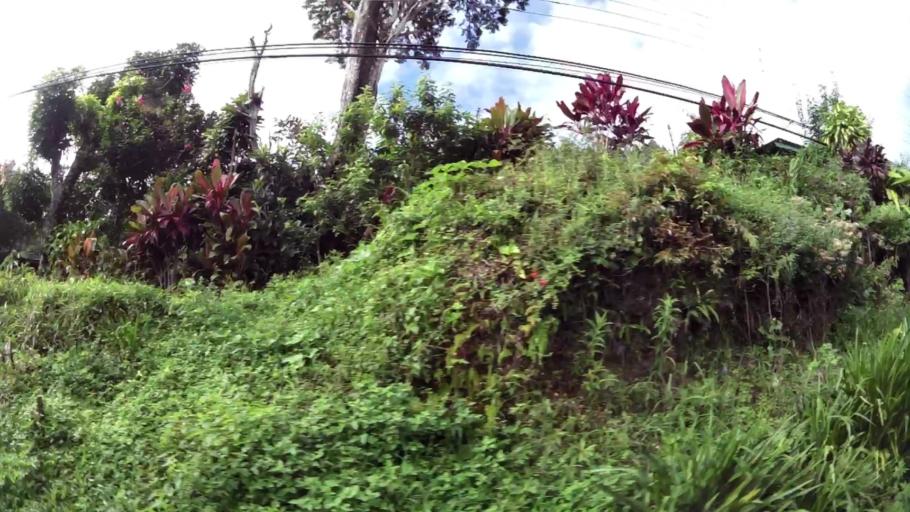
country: PA
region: Chiriqui
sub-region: Distrito Boquete
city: Boquete
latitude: 8.7901
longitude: -82.4412
